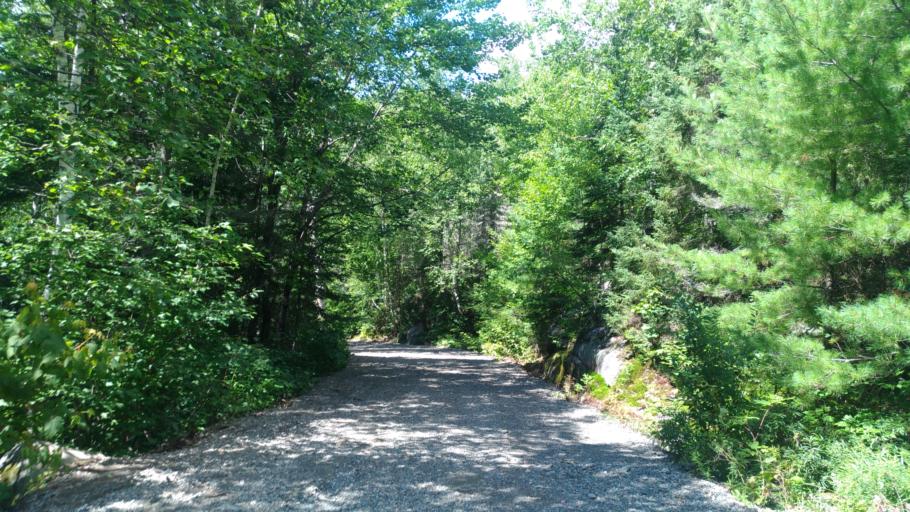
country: CA
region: Ontario
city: Rayside-Balfour
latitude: 46.5915
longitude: -81.5502
